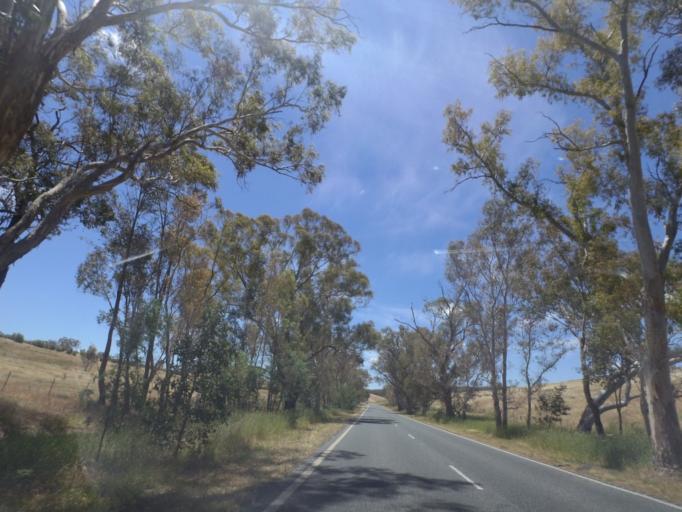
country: AU
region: Victoria
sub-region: Mount Alexander
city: Castlemaine
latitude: -37.1951
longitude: 144.1476
